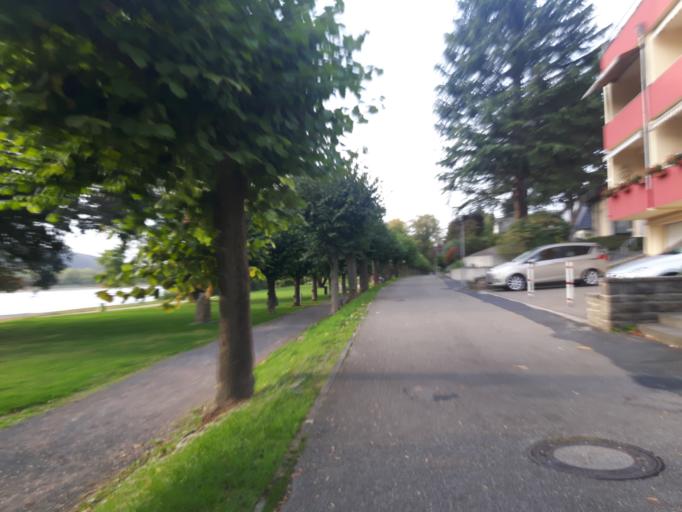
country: DE
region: Rheinland-Pfalz
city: Bad Honningen
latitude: 50.5179
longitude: 7.3027
